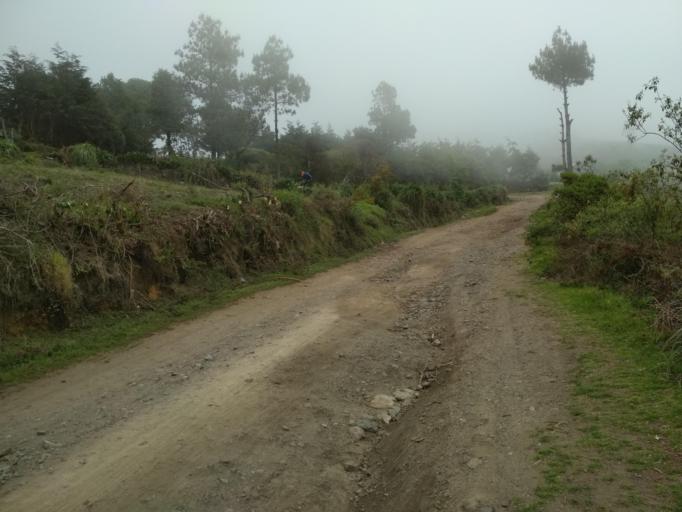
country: MX
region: Veracruz
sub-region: Mariano Escobedo
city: Texmola
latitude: 18.9606
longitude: -97.2191
